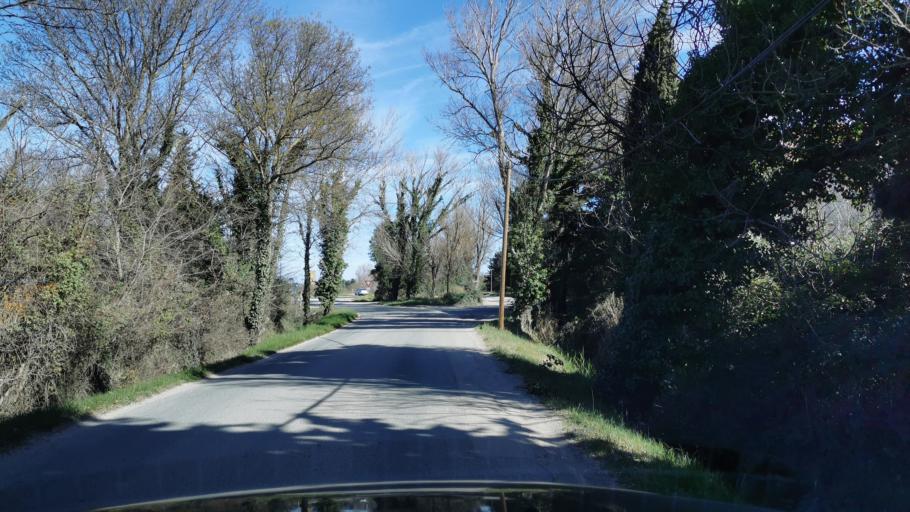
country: FR
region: Languedoc-Roussillon
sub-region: Departement de l'Aude
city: Narbonne
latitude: 43.1932
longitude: 2.9924
